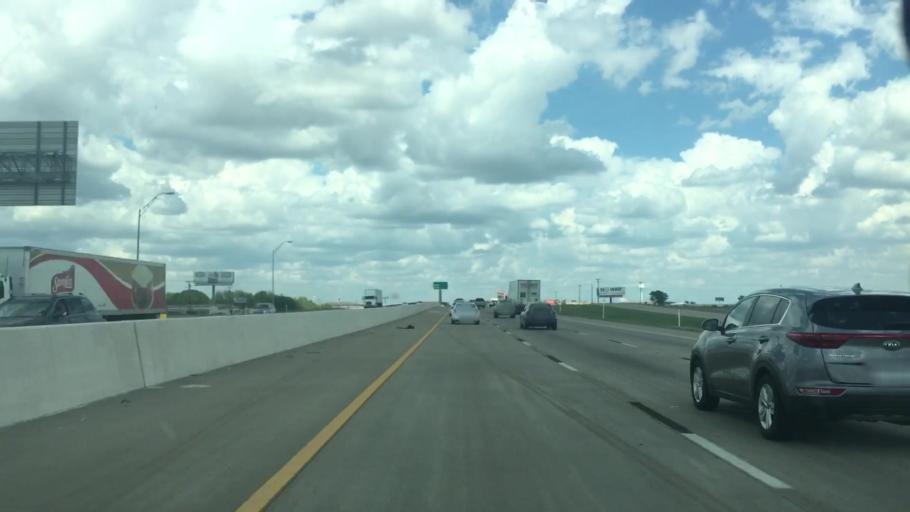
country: US
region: Texas
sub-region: McLennan County
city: Hewitt
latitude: 31.4479
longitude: -97.1780
